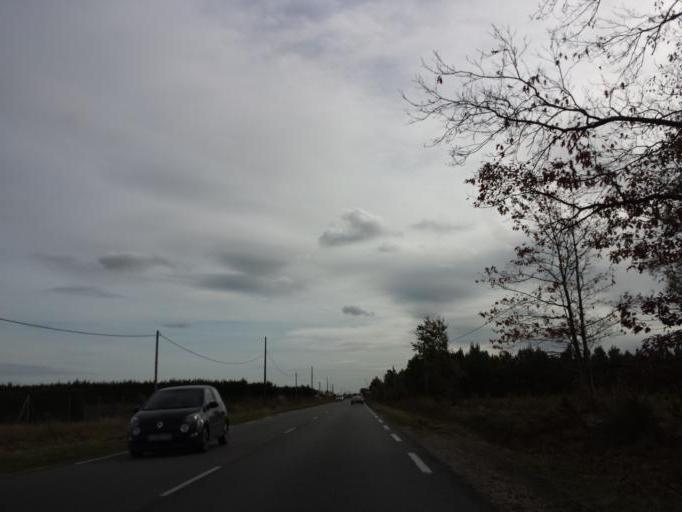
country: FR
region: Aquitaine
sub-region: Departement de la Gironde
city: Marcheprime
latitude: 44.7740
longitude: -0.9284
